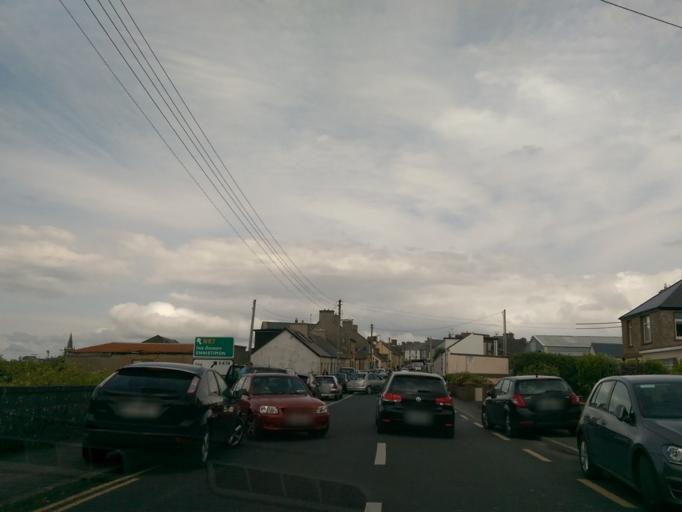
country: IE
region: Munster
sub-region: An Clar
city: Kilrush
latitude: 52.8535
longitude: -9.4043
